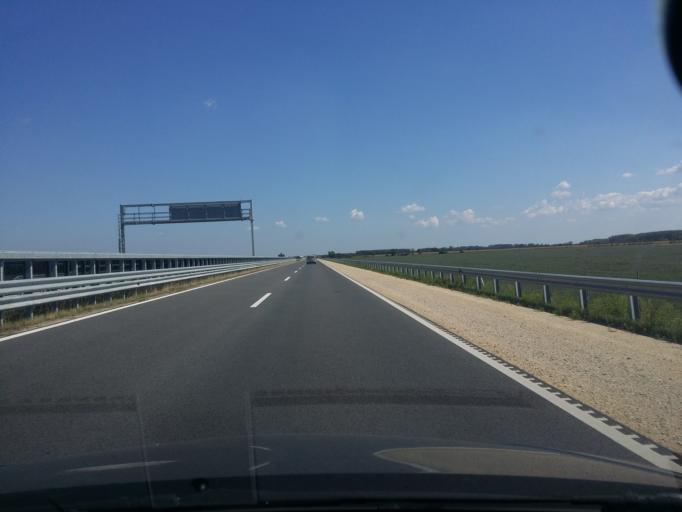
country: HU
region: Gyor-Moson-Sopron
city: Mihalyi
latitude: 47.5157
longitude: 17.1854
